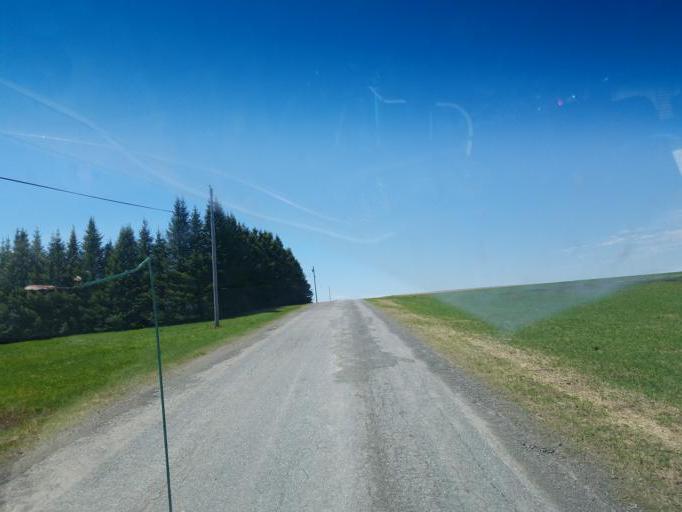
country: US
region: Maine
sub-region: Aroostook County
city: Caribou
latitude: 46.8675
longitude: -68.1927
